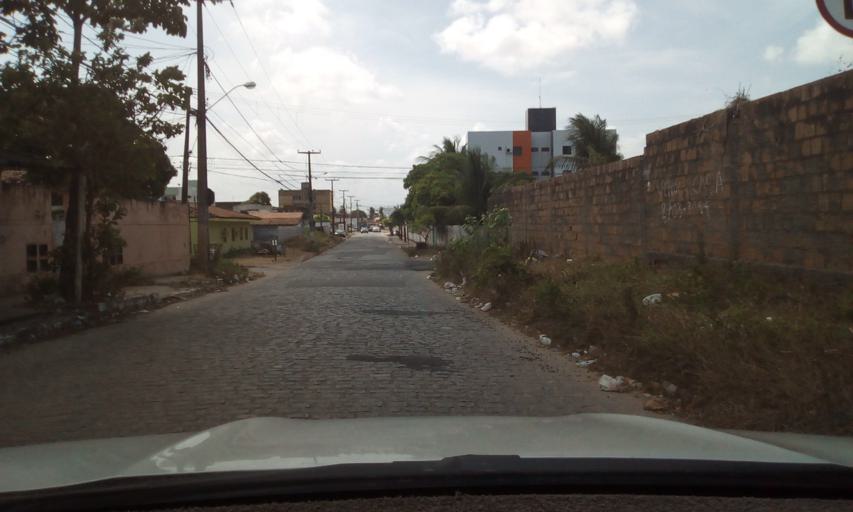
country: BR
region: Paraiba
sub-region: Joao Pessoa
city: Joao Pessoa
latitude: -7.1739
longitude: -34.8718
